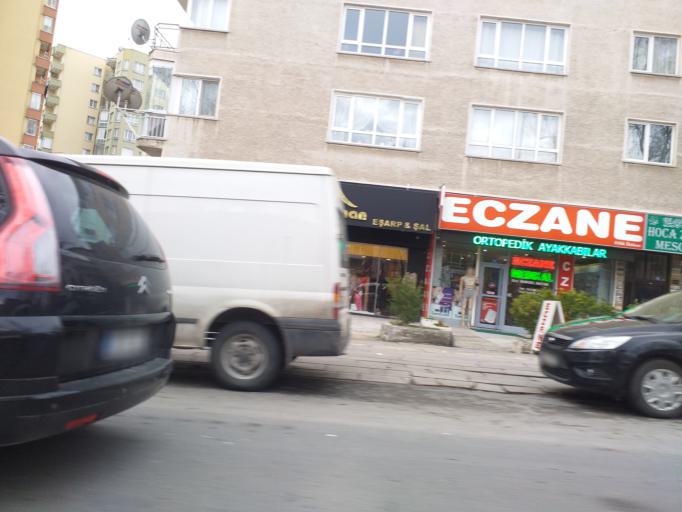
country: TR
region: Ankara
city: Ankara
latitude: 39.9710
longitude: 32.8336
